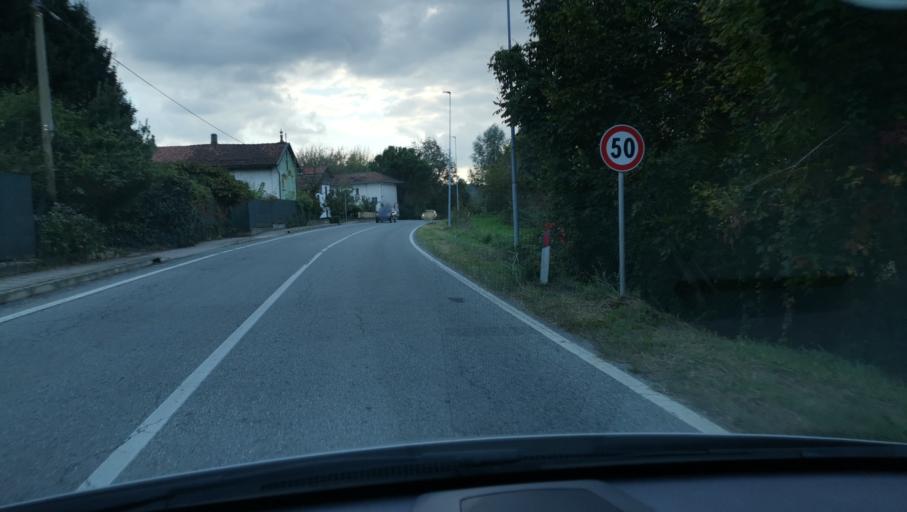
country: IT
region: Piedmont
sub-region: Provincia di Torino
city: Piana San Raffaele
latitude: 45.1537
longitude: 7.8520
